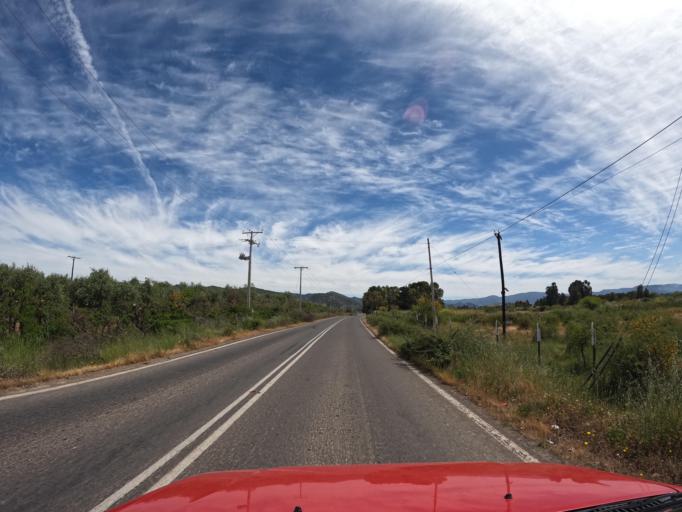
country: CL
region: Maule
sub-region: Provincia de Talca
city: Talca
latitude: -35.1109
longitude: -71.6301
